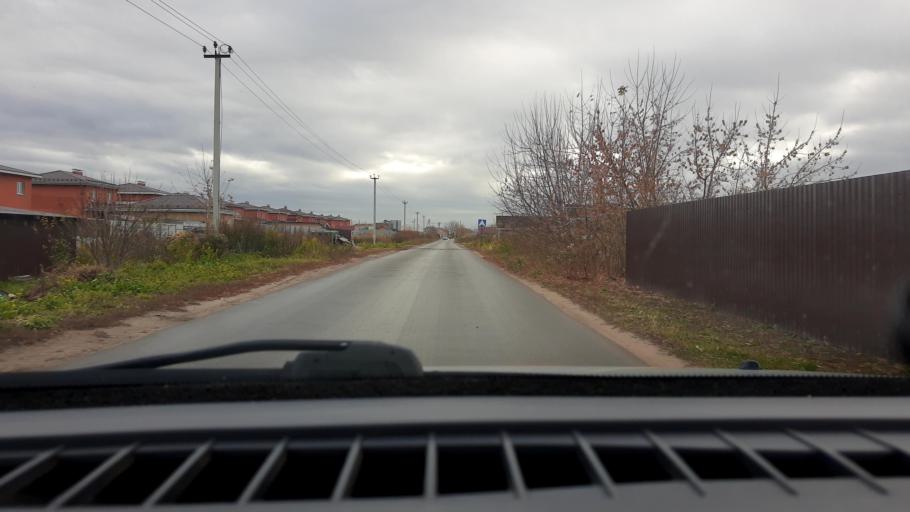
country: RU
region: Nizjnij Novgorod
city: Afonino
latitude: 56.2042
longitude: 44.1299
